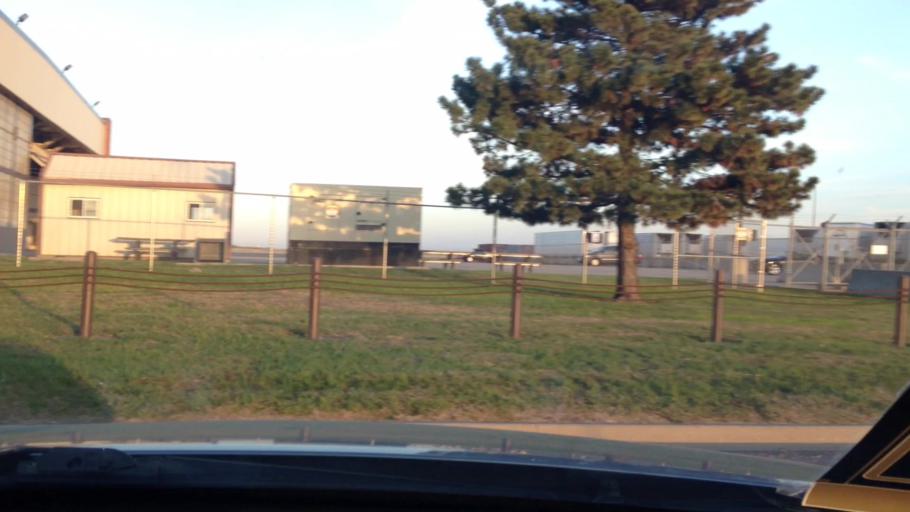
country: US
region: Kansas
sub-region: Johnson County
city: Gardner
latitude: 38.8357
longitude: -94.8961
